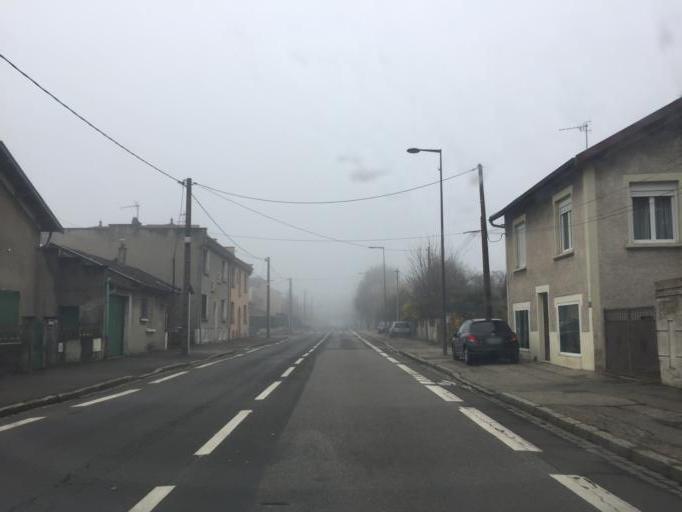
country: FR
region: Rhone-Alpes
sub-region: Departement du Rhone
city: Sathonay-Camp
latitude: 45.8017
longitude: 4.8665
